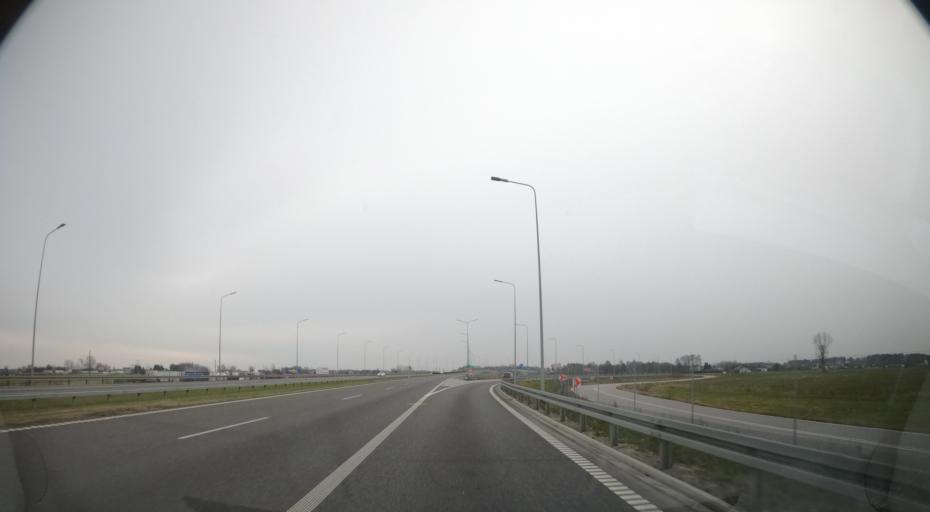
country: PL
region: Masovian Voivodeship
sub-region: Powiat radomski
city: Jedlinsk
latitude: 51.5357
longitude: 21.0733
